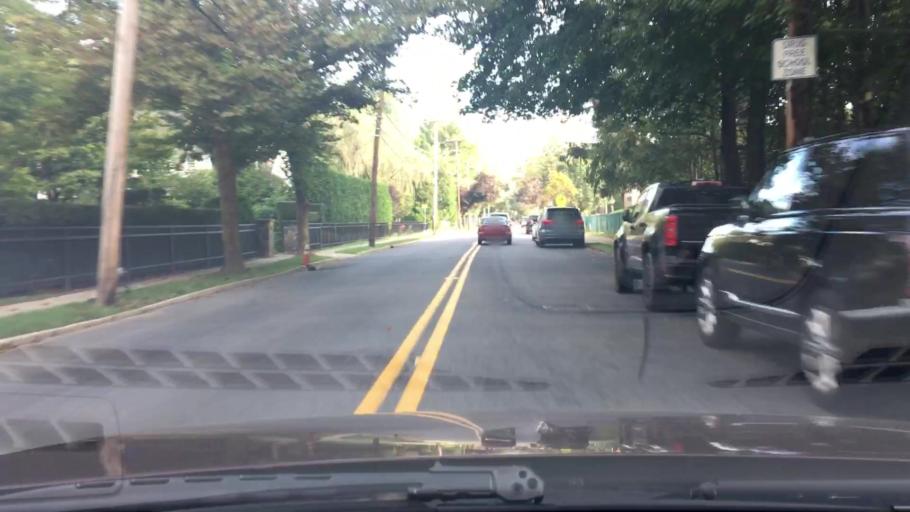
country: US
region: New York
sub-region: Westchester County
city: Rye
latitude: 40.9733
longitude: -73.6819
